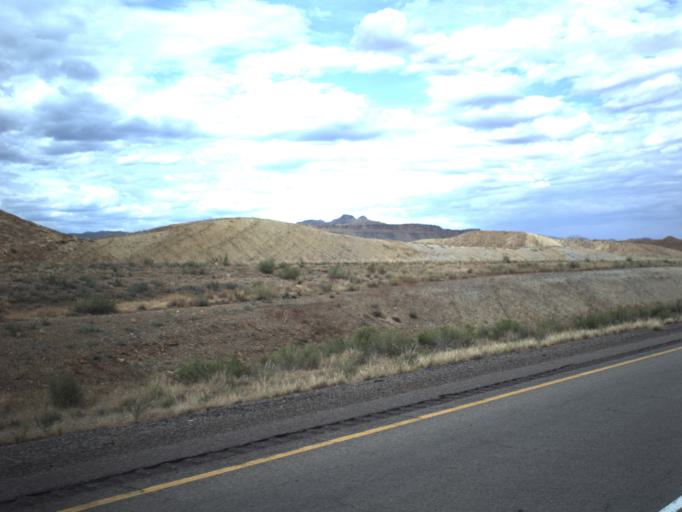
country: US
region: Utah
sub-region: Grand County
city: Moab
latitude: 38.9343
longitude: -109.8477
